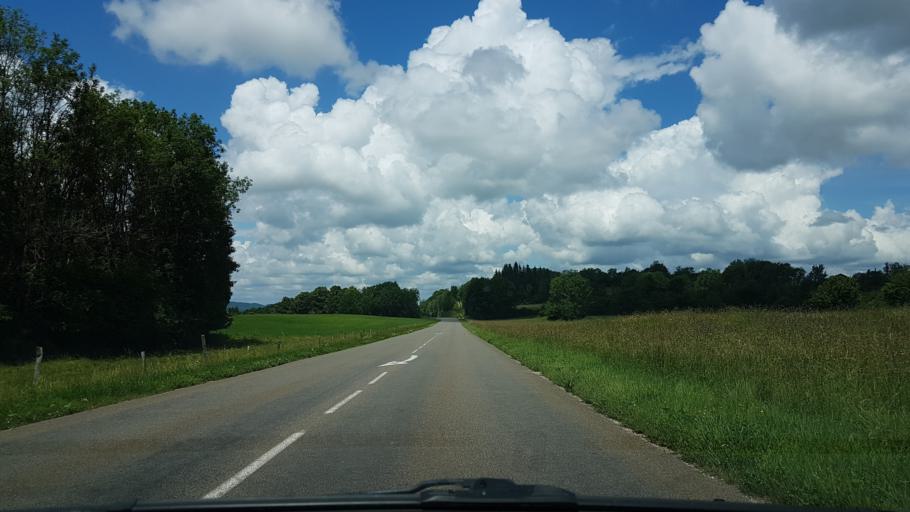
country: FR
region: Franche-Comte
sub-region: Departement du Jura
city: Clairvaux-les-Lacs
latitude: 46.5439
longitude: 5.7497
